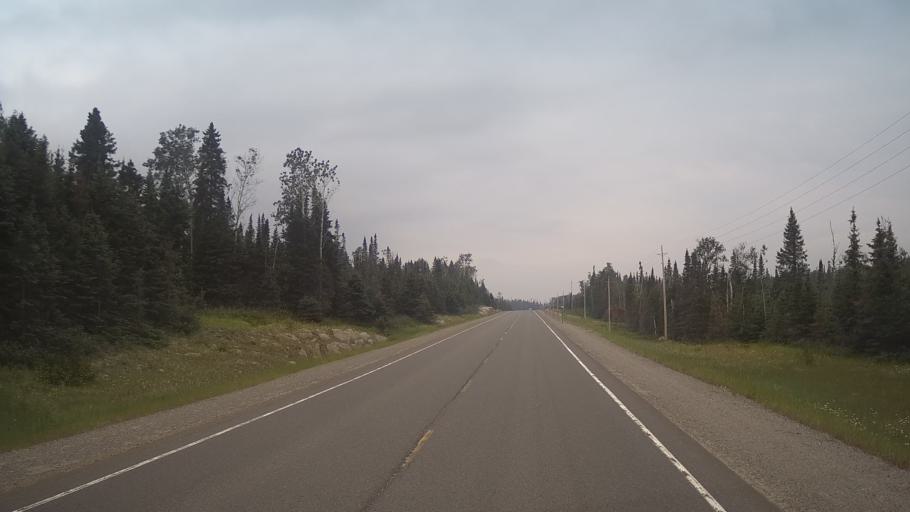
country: CA
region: Ontario
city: Greenstone
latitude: 49.5286
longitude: -88.0128
